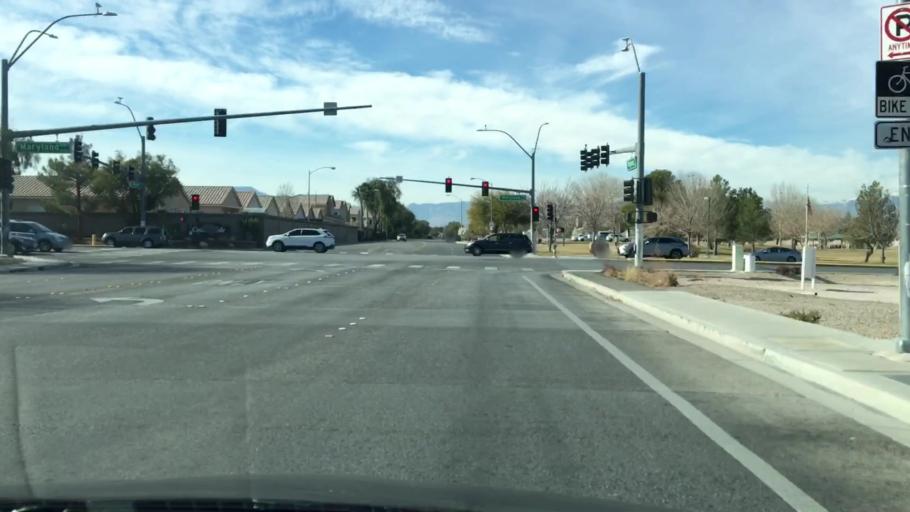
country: US
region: Nevada
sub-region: Clark County
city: Whitney
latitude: 36.0354
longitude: -115.1356
